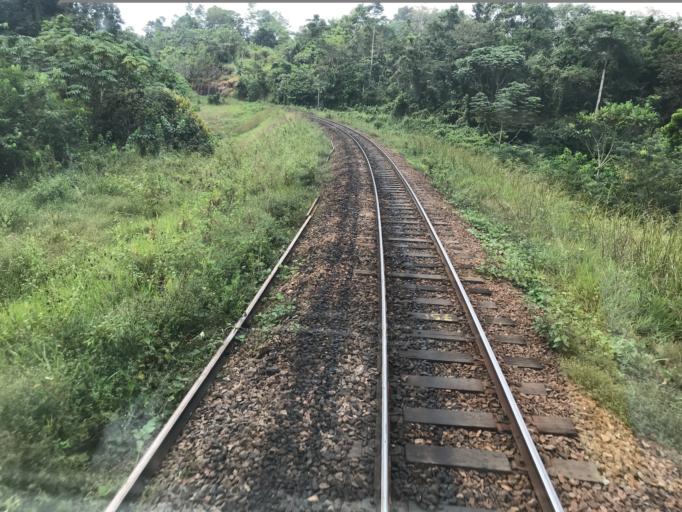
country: CM
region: Centre
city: Eseka
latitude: 3.5812
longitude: 10.8981
